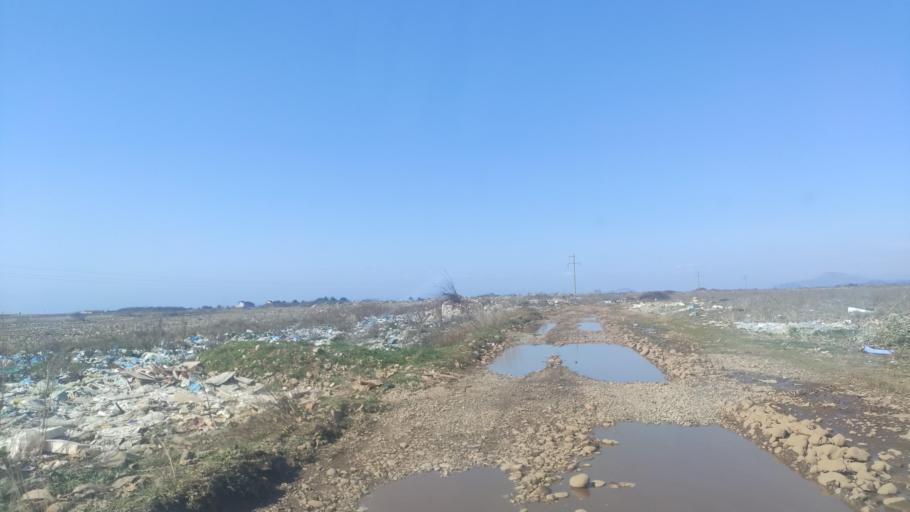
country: AL
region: Shkoder
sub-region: Rrethi i Malesia e Madhe
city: Koplik
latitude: 42.2279
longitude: 19.4375
